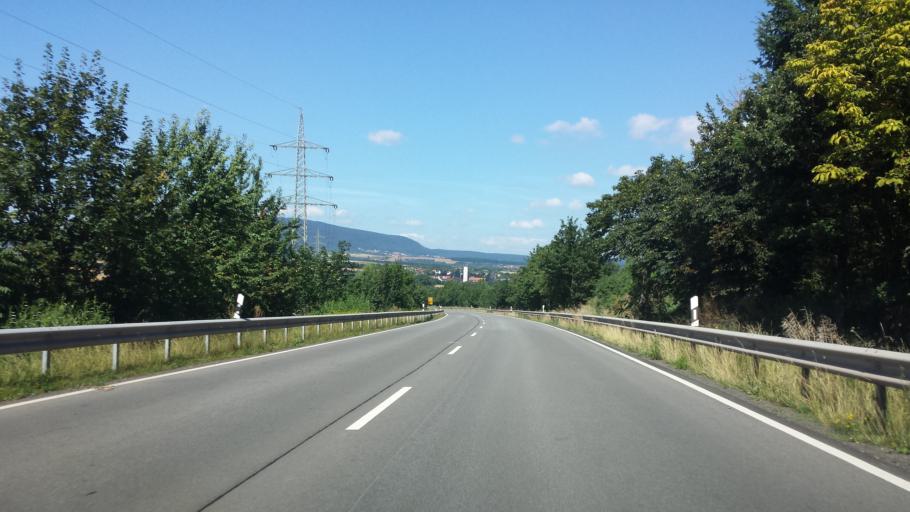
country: DE
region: Rheinland-Pfalz
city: Gollheim
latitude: 49.5924
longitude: 8.0367
